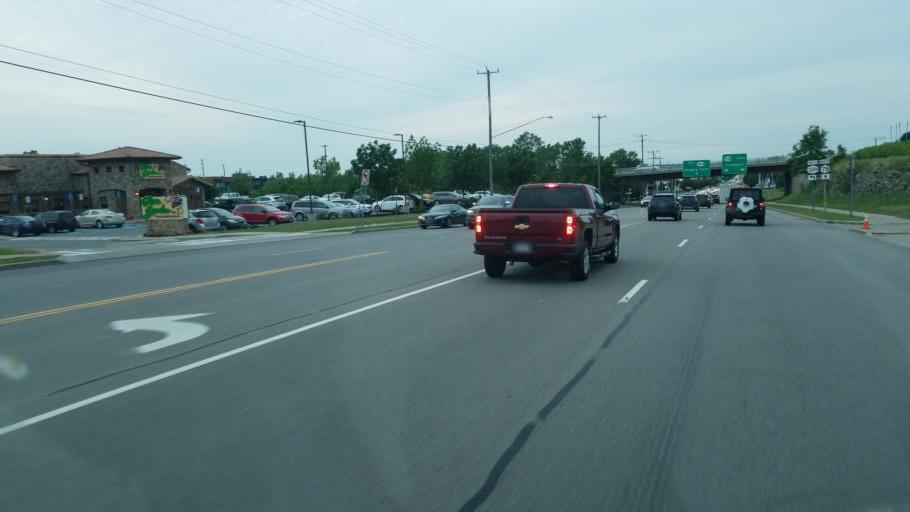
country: US
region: New York
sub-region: Erie County
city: Harris Hill
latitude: 42.9768
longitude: -78.6968
